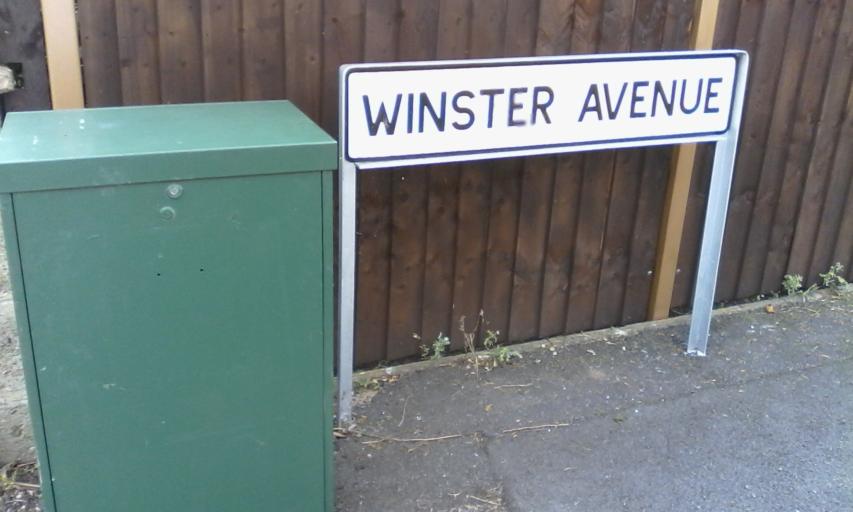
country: GB
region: England
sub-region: Nottinghamshire
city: Arnold
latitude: 52.9722
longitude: -1.0929
